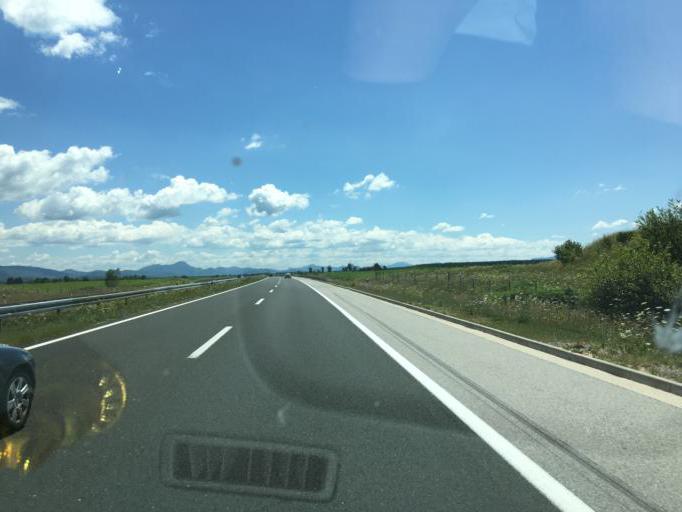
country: HR
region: Licko-Senjska
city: Gospic
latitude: 44.5238
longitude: 15.4584
